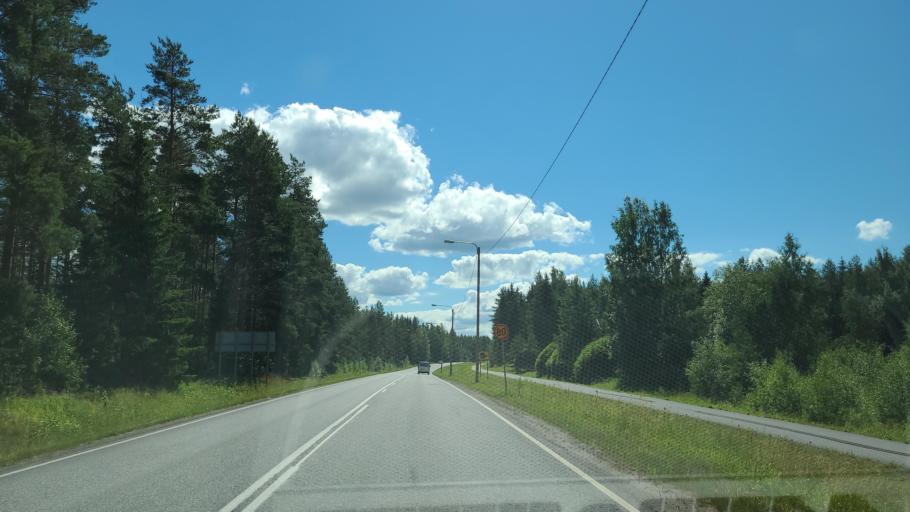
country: FI
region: Southern Ostrobothnia
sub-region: Seinaejoki
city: Seinaejoki
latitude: 62.8403
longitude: 22.7970
